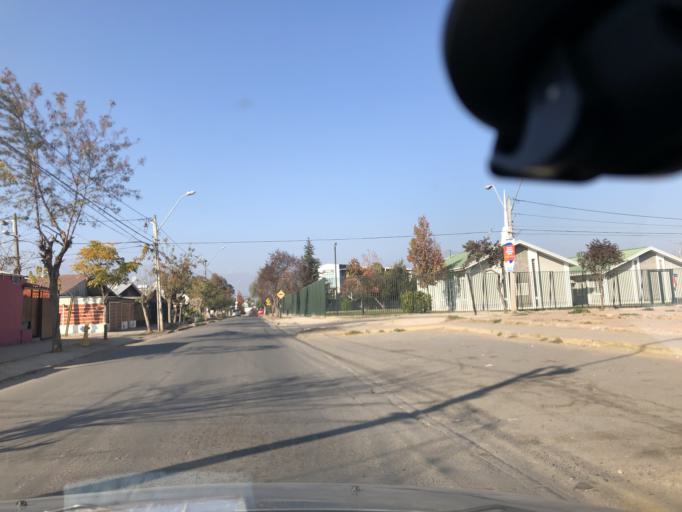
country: CL
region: Santiago Metropolitan
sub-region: Provincia de Cordillera
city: Puente Alto
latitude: -33.6235
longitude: -70.5920
